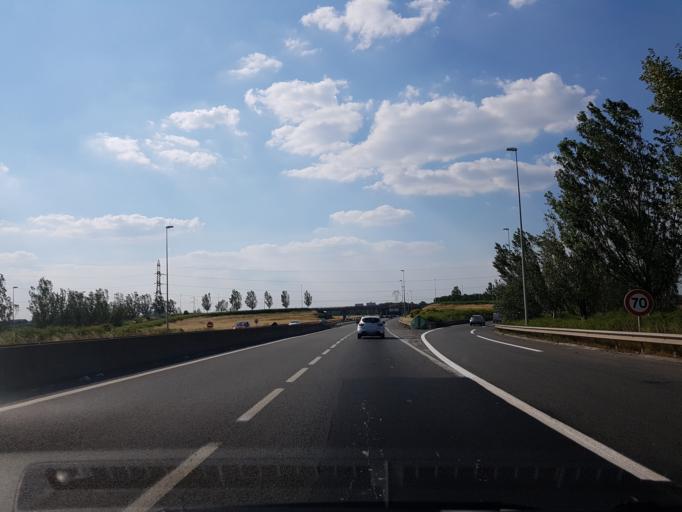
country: FR
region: Nord-Pas-de-Calais
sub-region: Departement du Nord
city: Auby
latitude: 50.4075
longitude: 3.0395
